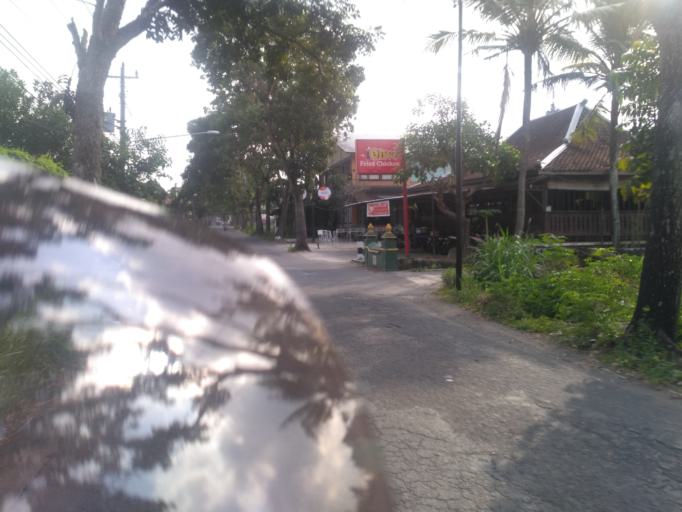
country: ID
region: Daerah Istimewa Yogyakarta
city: Yogyakarta
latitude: -7.7761
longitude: 110.3418
